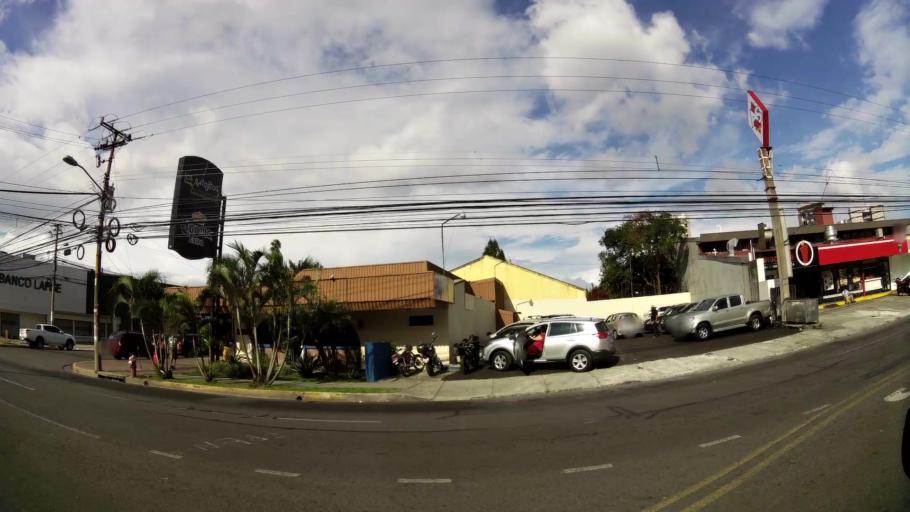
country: CR
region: San Jose
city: San Rafael
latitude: 9.9378
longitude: -84.1144
